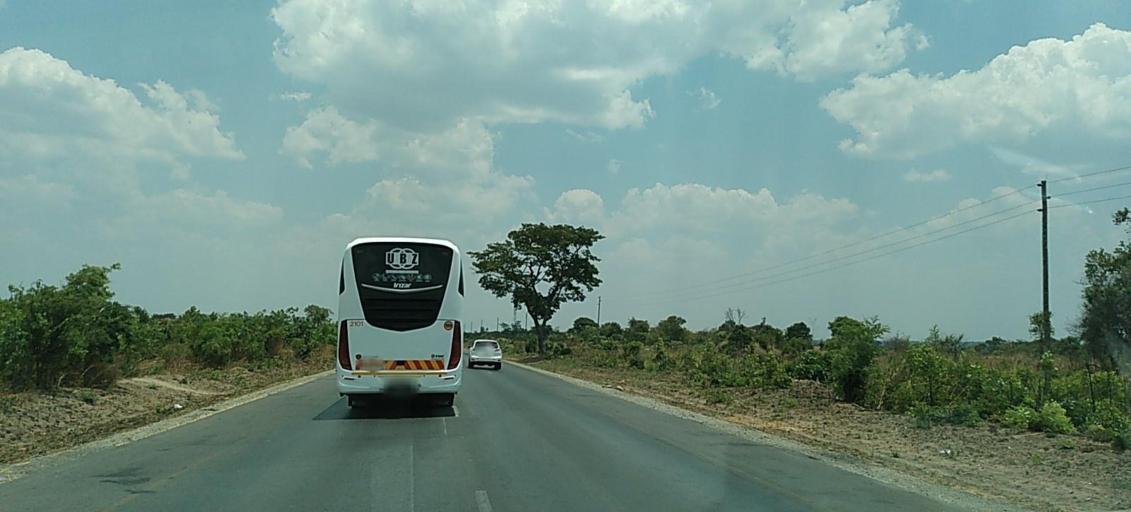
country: ZM
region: Central
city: Kapiri Mposhi
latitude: -14.0606
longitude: 28.6450
